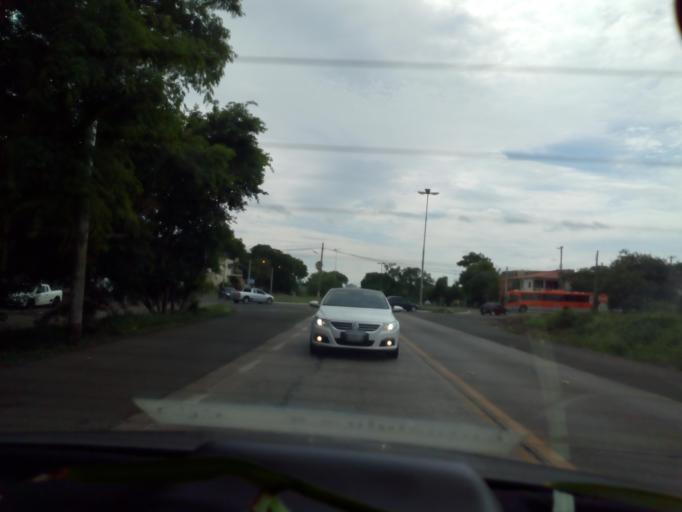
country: BR
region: Rio Grande do Sul
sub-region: Uruguaiana
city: Uruguaiana
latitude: -29.7480
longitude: -57.0780
